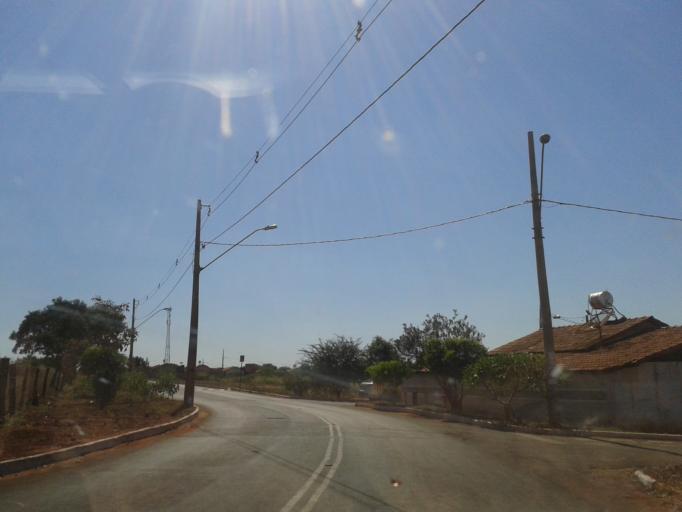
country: BR
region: Minas Gerais
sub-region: Ituiutaba
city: Ituiutaba
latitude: -19.0103
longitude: -49.4827
